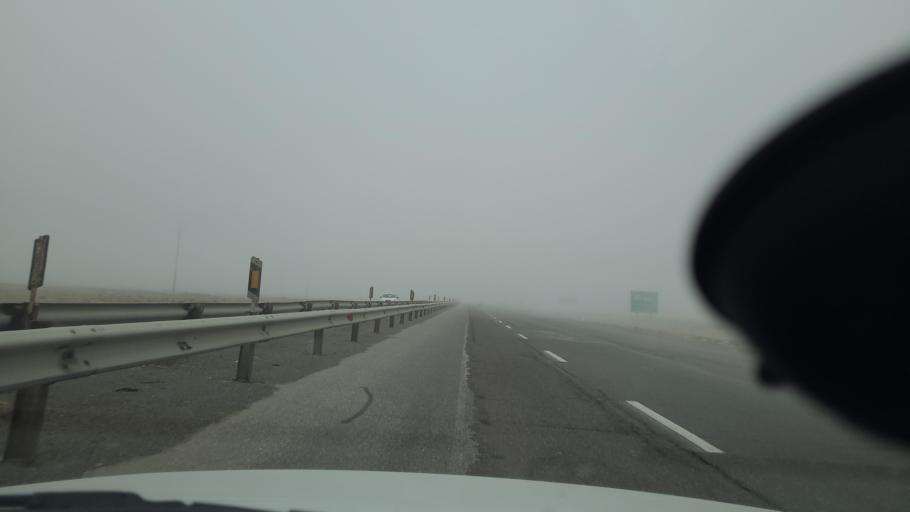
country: IR
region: Razavi Khorasan
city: Fariman
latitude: 35.7829
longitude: 59.7396
